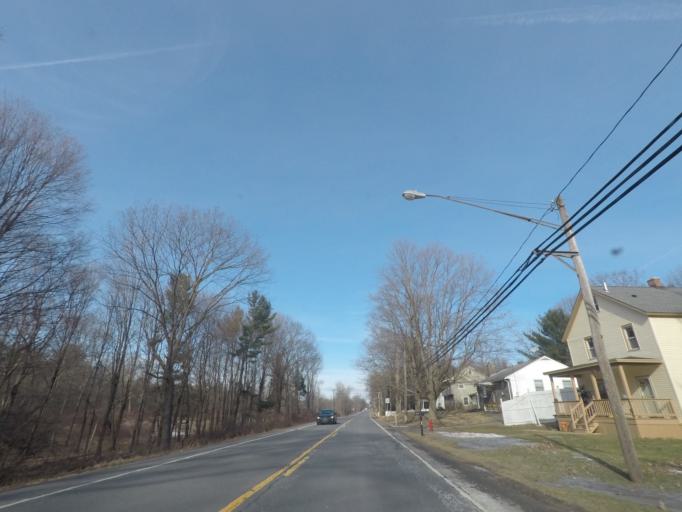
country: US
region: New York
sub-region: Rensselaer County
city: Nassau
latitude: 42.5084
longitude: -73.6132
